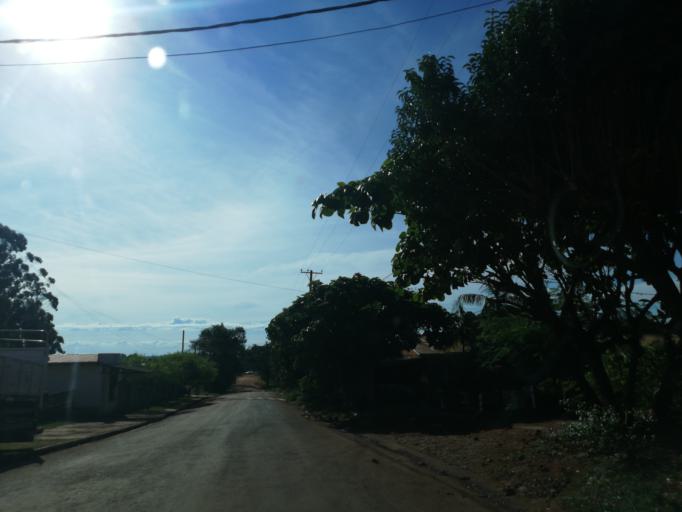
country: AR
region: Misiones
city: Dos de Mayo
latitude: -26.9934
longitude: -54.4949
